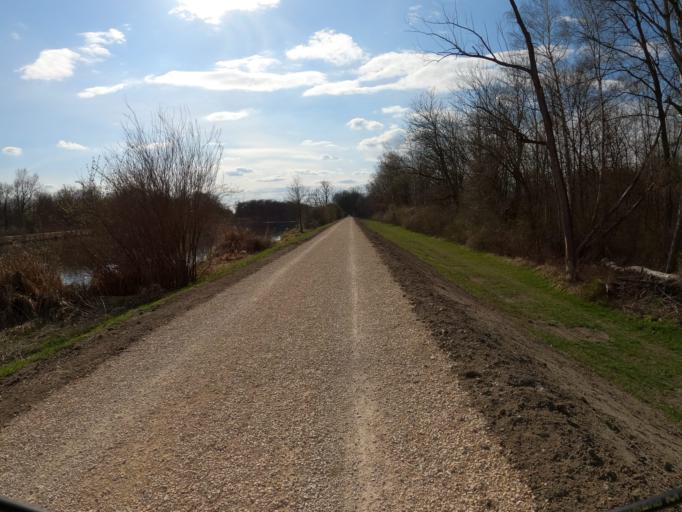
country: DE
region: Bavaria
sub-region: Swabia
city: Nersingen
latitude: 48.4362
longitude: 10.0767
